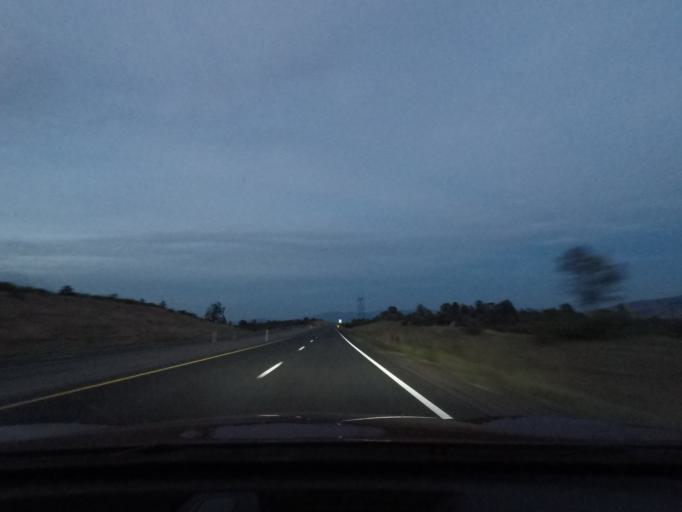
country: US
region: Arizona
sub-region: Yavapai County
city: Prescott
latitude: 34.6148
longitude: -112.4751
